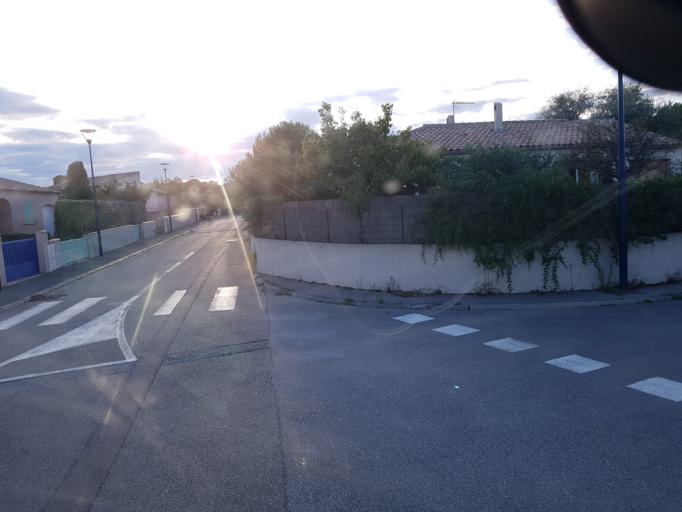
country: FR
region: Languedoc-Roussillon
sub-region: Departement de l'Aude
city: Leucate
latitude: 42.9370
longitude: 3.0269
